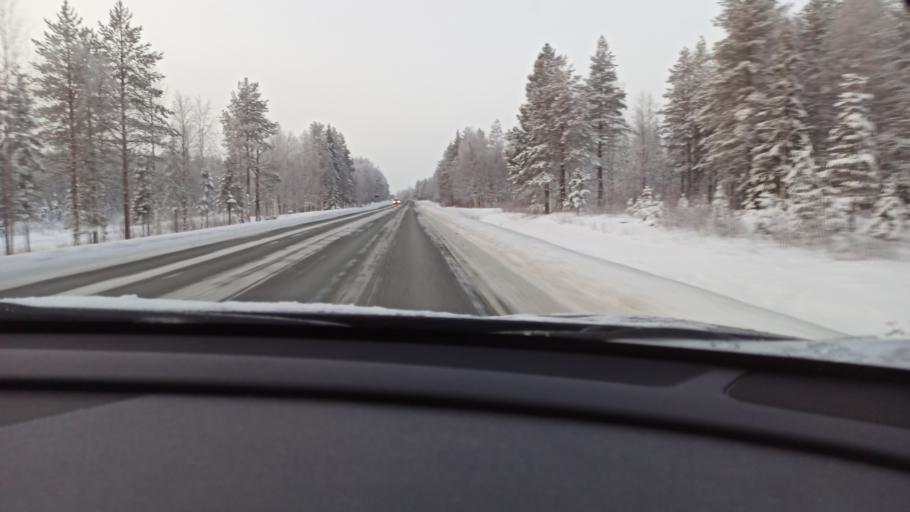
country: FI
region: Lapland
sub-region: Rovaniemi
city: Rovaniemi
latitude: 66.5487
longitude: 25.8760
